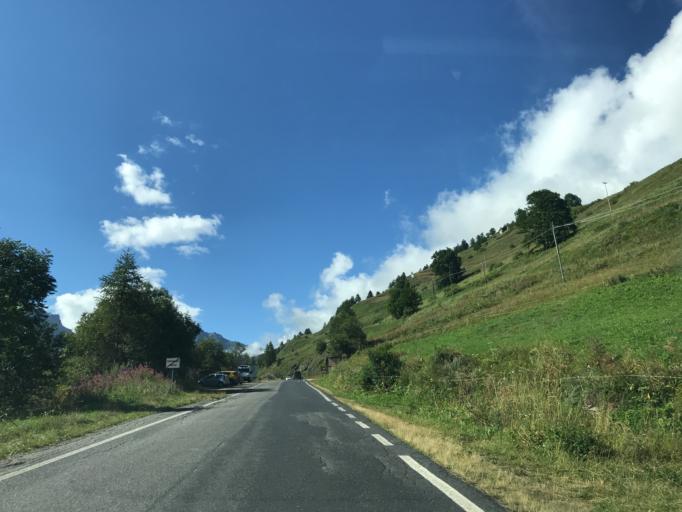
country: IT
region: Piedmont
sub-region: Provincia di Cuneo
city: Pontechianale
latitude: 44.6260
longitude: 7.0232
